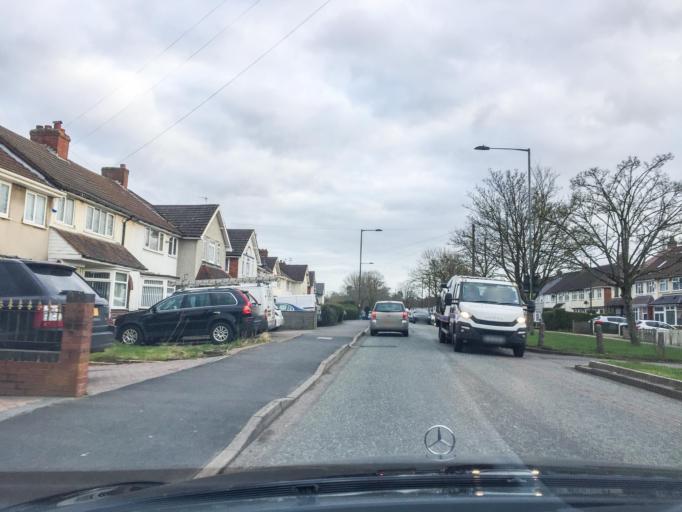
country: GB
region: England
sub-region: Worcestershire
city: Alvechurch
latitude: 52.3931
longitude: -1.9605
